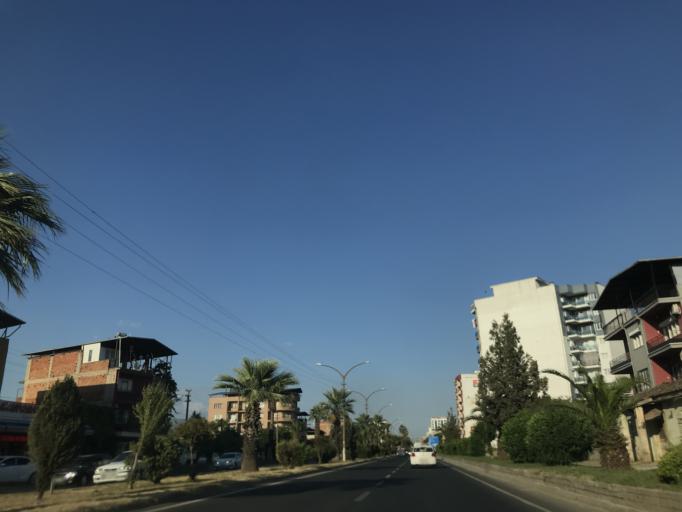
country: TR
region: Aydin
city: Umurlu
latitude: 37.8501
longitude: 27.9543
